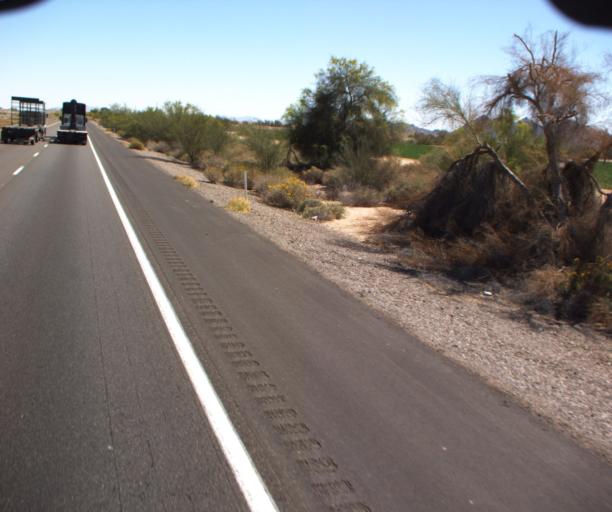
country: US
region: Arizona
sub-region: Yuma County
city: Wellton
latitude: 32.6752
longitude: -114.0609
